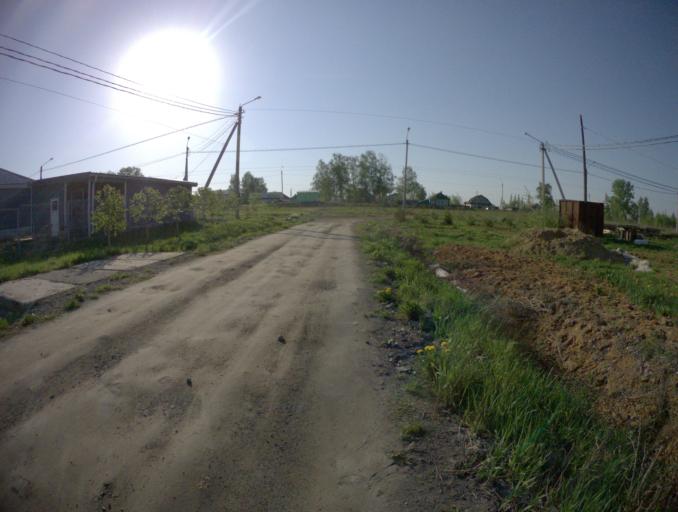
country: RU
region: Vladimir
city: Novovyazniki
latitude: 56.2249
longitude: 42.1869
